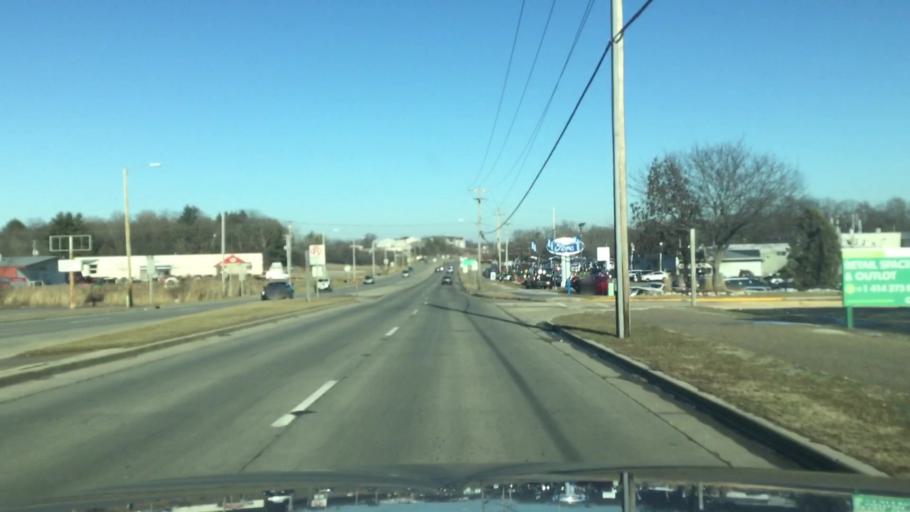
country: US
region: Wisconsin
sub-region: Racine County
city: Burlington
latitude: 42.6930
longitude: -88.2646
